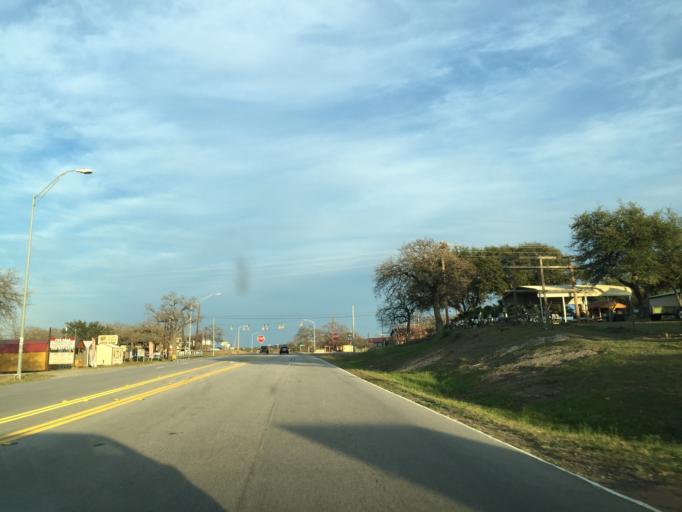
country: US
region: Texas
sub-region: Llano County
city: Buchanan Dam
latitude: 30.7332
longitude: -98.4674
